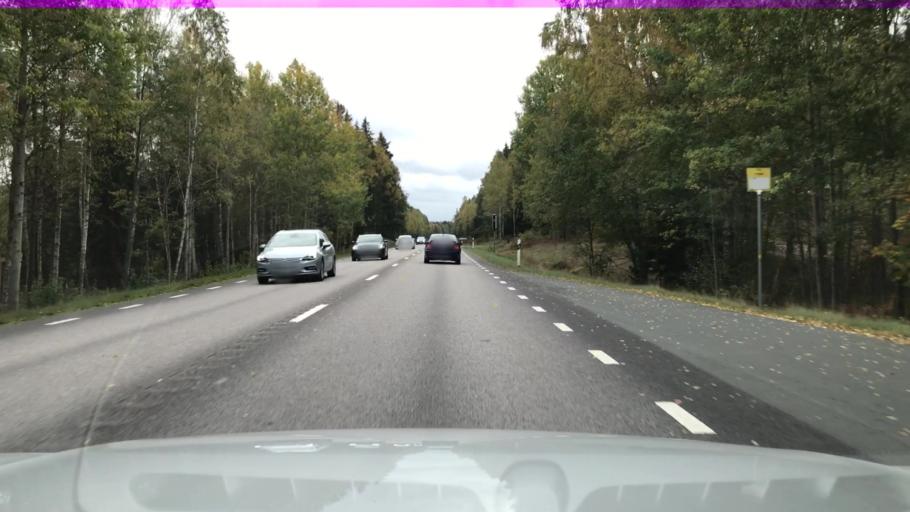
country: SE
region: Kalmar
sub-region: Hultsfreds Kommun
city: Hultsfred
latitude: 57.5495
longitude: 15.8454
